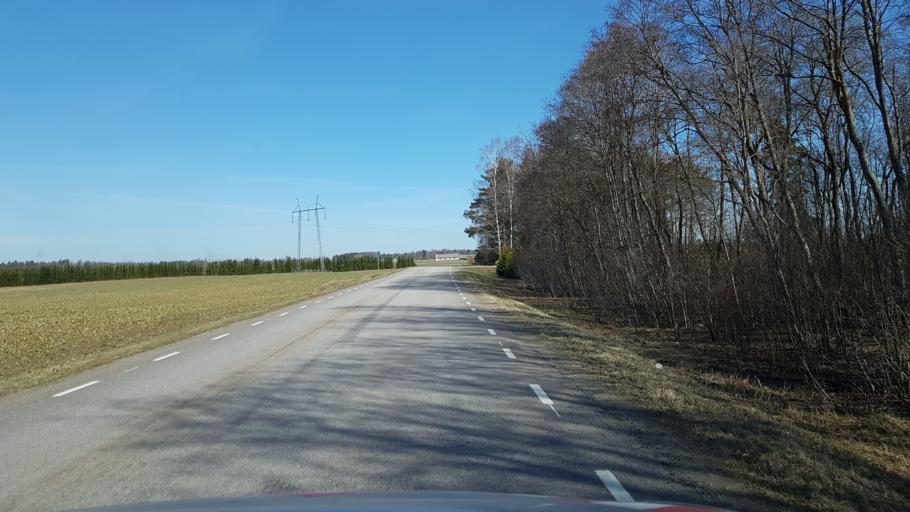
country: EE
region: Laeaene-Virumaa
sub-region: Vinni vald
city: Vinni
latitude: 59.2436
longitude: 26.3521
